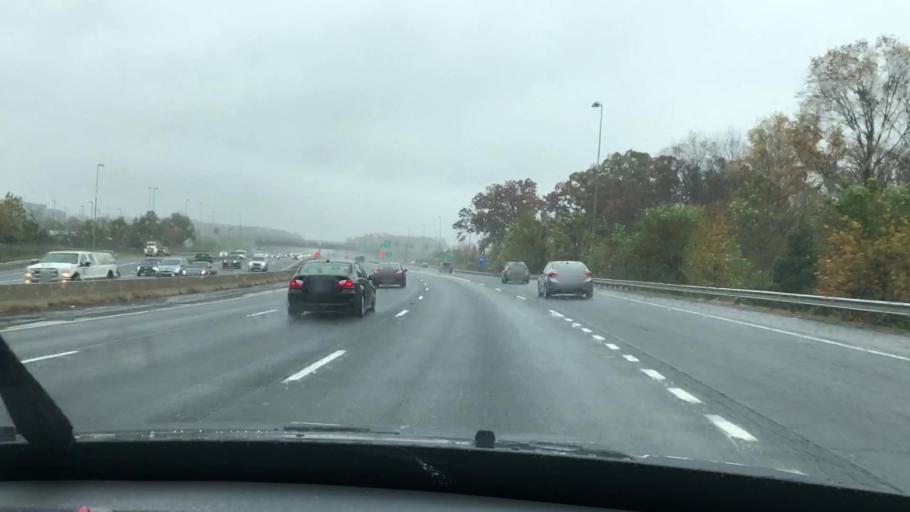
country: US
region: Virginia
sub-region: Fairfax County
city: Chantilly
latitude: 38.8782
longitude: -77.4490
